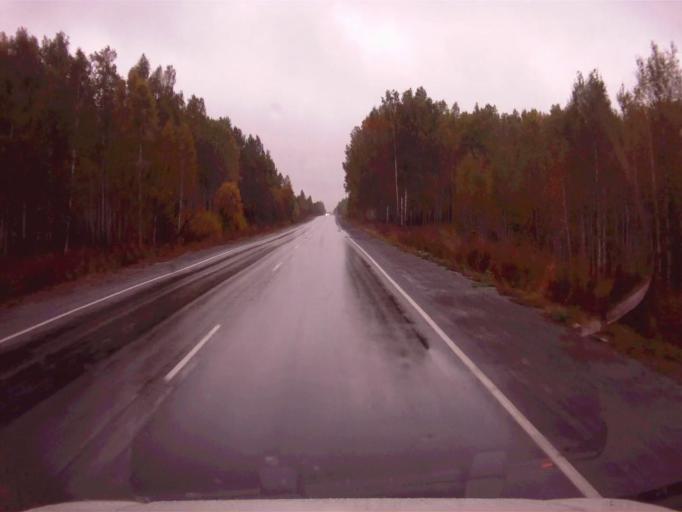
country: RU
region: Chelyabinsk
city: Tayginka
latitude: 55.5353
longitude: 60.6467
